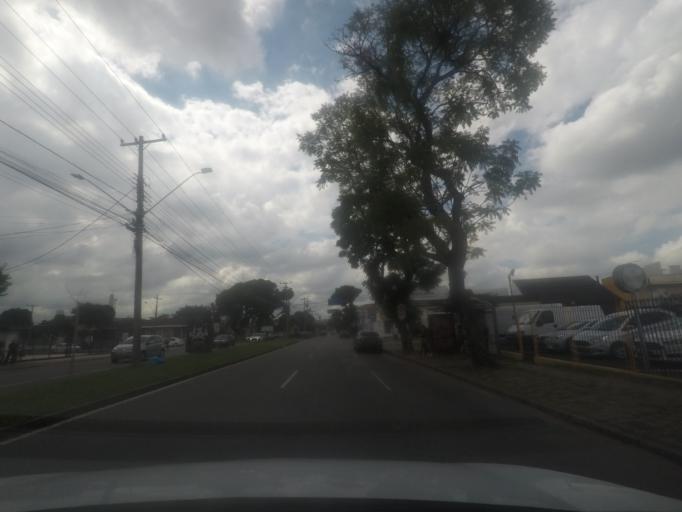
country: BR
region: Parana
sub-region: Curitiba
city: Curitiba
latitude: -25.4532
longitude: -49.2649
